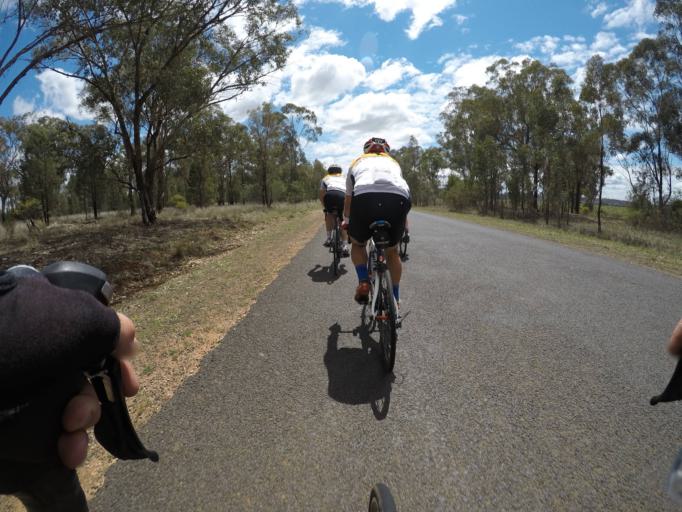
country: AU
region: New South Wales
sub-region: Dubbo Municipality
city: Dubbo
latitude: -32.3998
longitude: 148.5713
